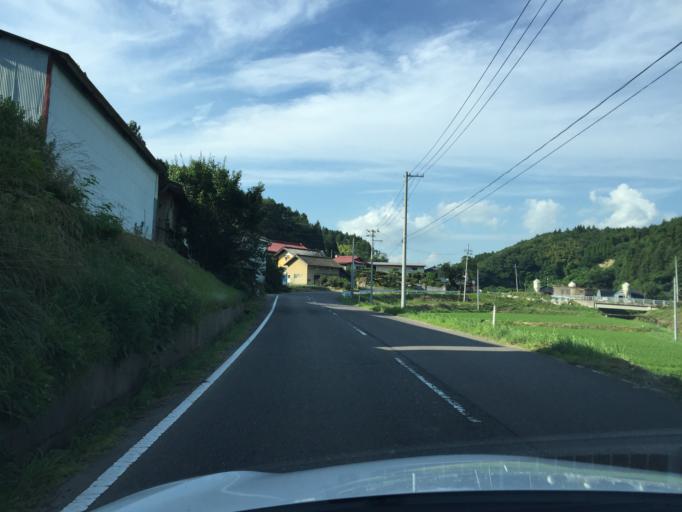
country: JP
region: Fukushima
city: Miharu
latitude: 37.3329
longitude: 140.5009
